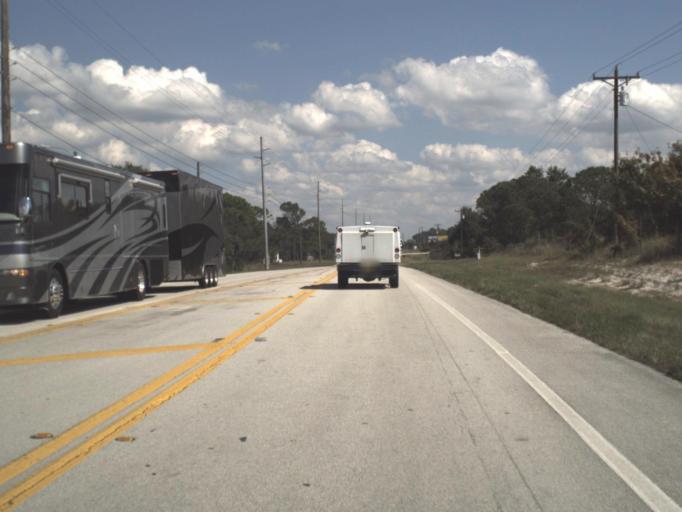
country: US
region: Florida
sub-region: Highlands County
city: Sebring
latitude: 27.4321
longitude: -81.3801
